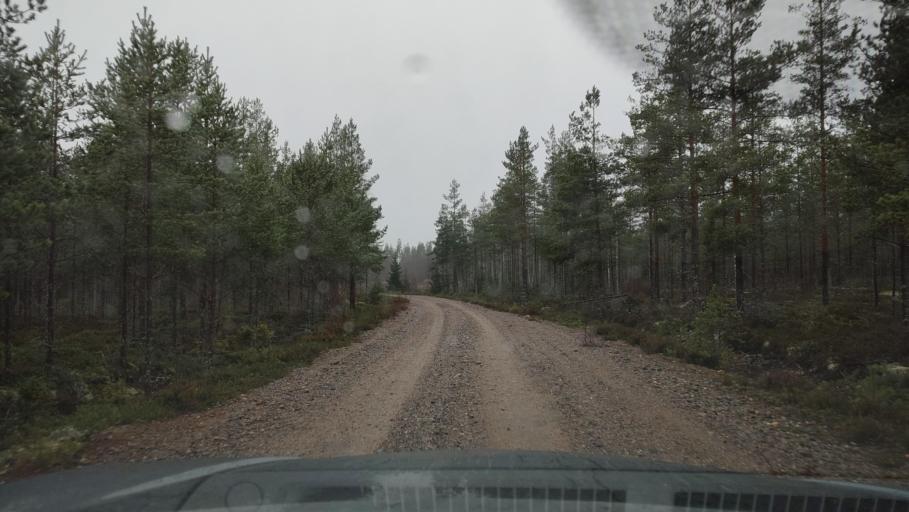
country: FI
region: Southern Ostrobothnia
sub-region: Suupohja
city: Karijoki
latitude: 62.1880
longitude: 21.7392
